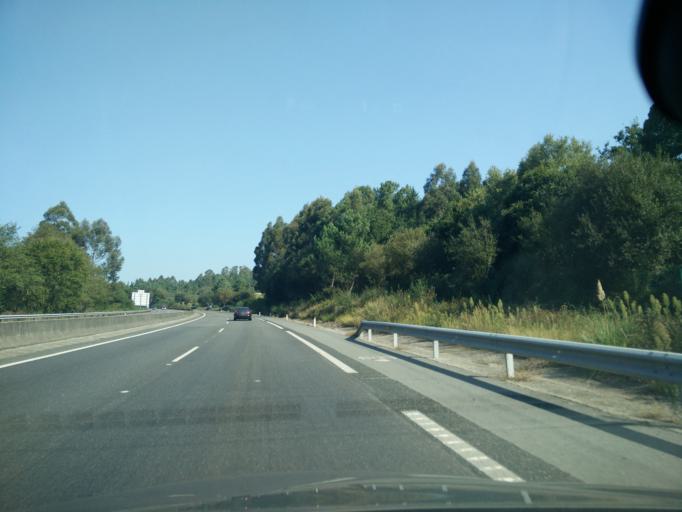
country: ES
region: Galicia
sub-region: Provincia da Coruna
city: Mino
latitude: 43.3828
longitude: -8.1786
